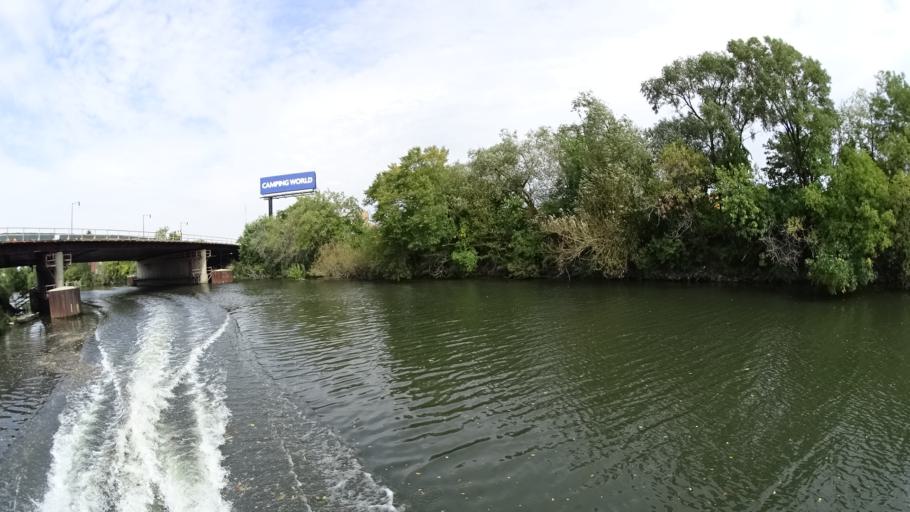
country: US
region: Illinois
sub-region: Cook County
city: Lincolnwood
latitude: 41.9355
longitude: -87.6874
